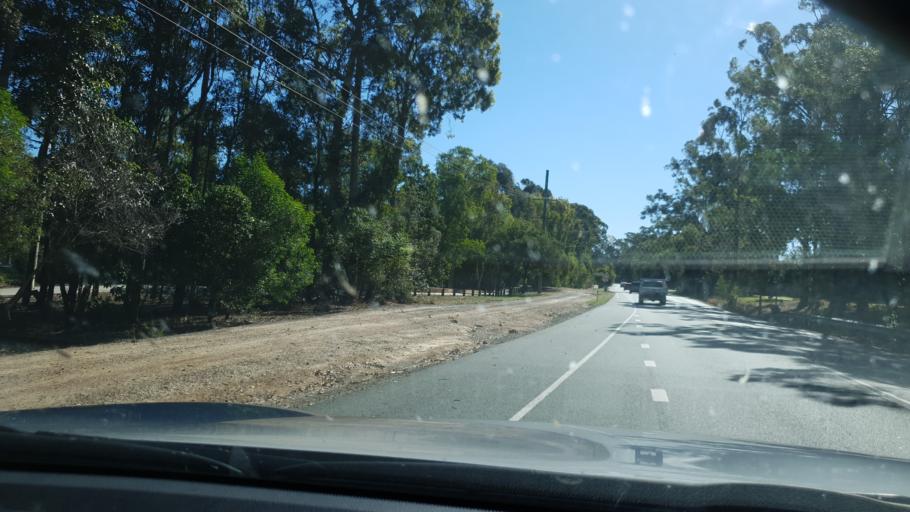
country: AU
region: Queensland
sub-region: Brisbane
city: Bridegman Downs
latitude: -27.3332
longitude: 152.9557
